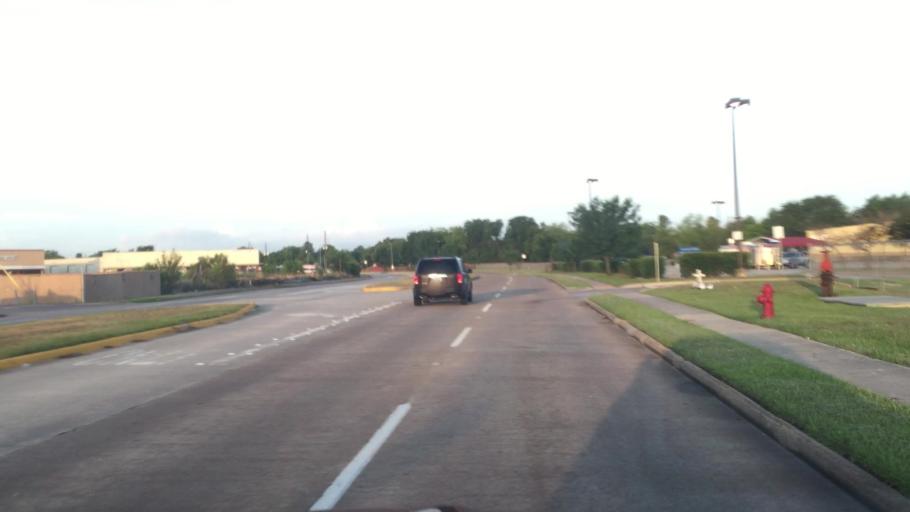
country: US
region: Texas
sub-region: Harris County
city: Hudson
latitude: 29.9605
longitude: -95.4790
